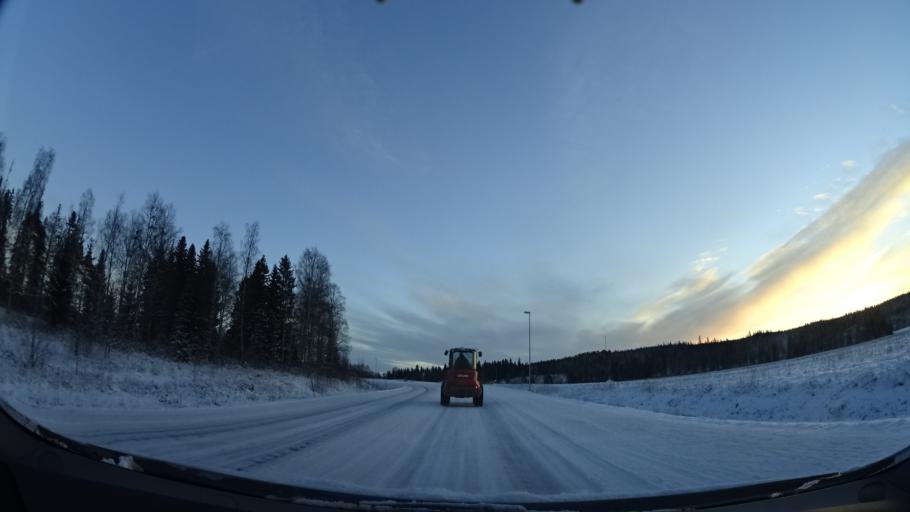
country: SE
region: Vaesterbotten
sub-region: Skelleftea Kommun
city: Kage
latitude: 64.8292
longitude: 21.0096
